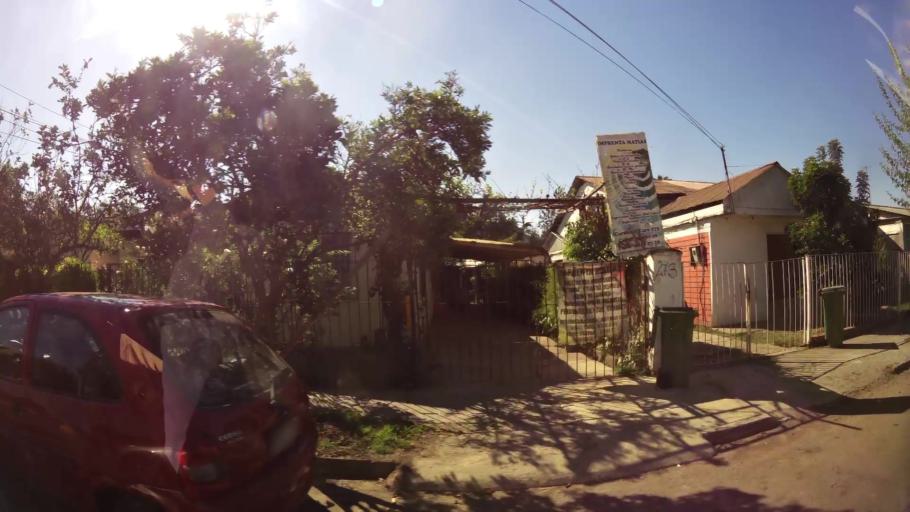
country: CL
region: Santiago Metropolitan
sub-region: Provincia de Talagante
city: Penaflor
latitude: -33.6051
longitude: -70.8987
